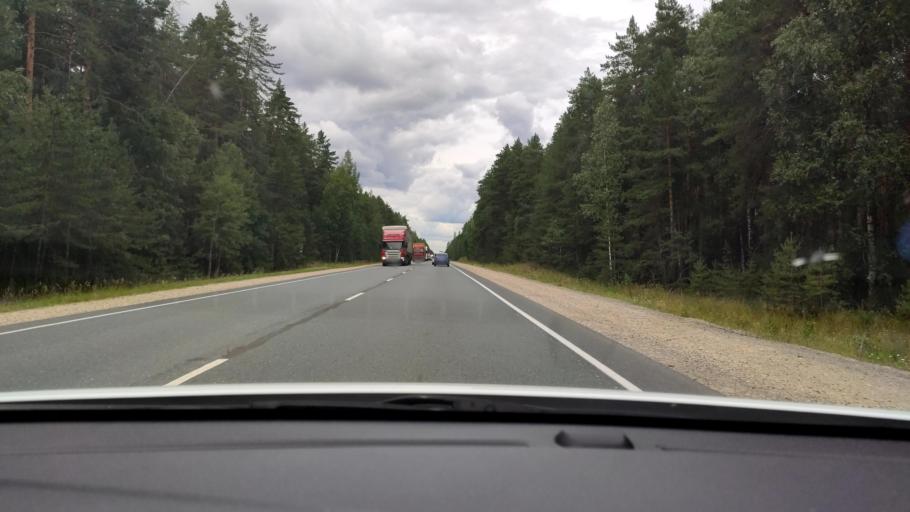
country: RU
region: Mariy-El
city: Pomary
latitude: 56.0347
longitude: 48.3808
